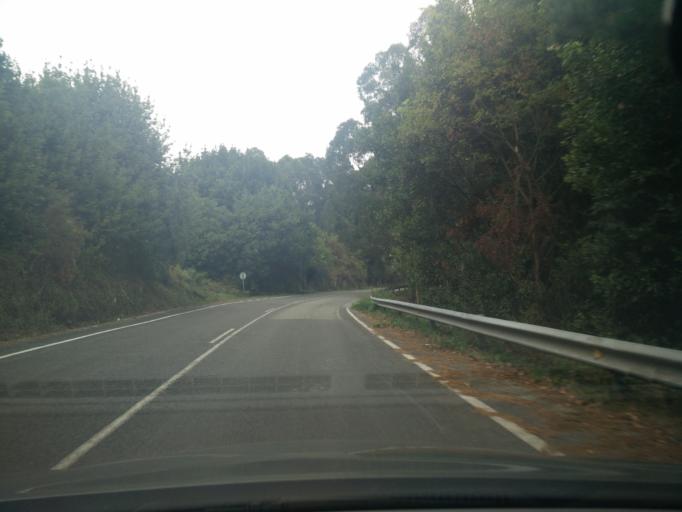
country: ES
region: Galicia
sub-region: Provincia da Coruna
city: Laxe
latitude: 43.2470
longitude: -8.9391
